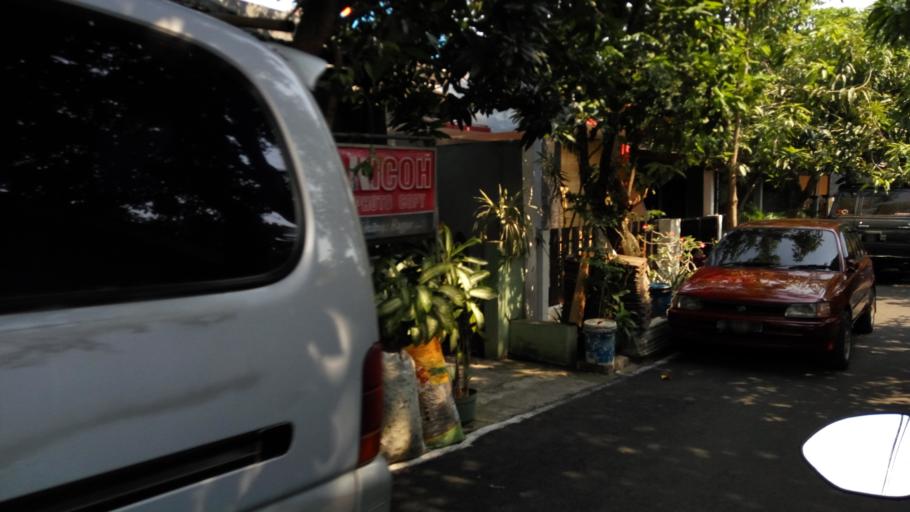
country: ID
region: Central Java
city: Mranggen
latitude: -7.0325
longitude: 110.4724
